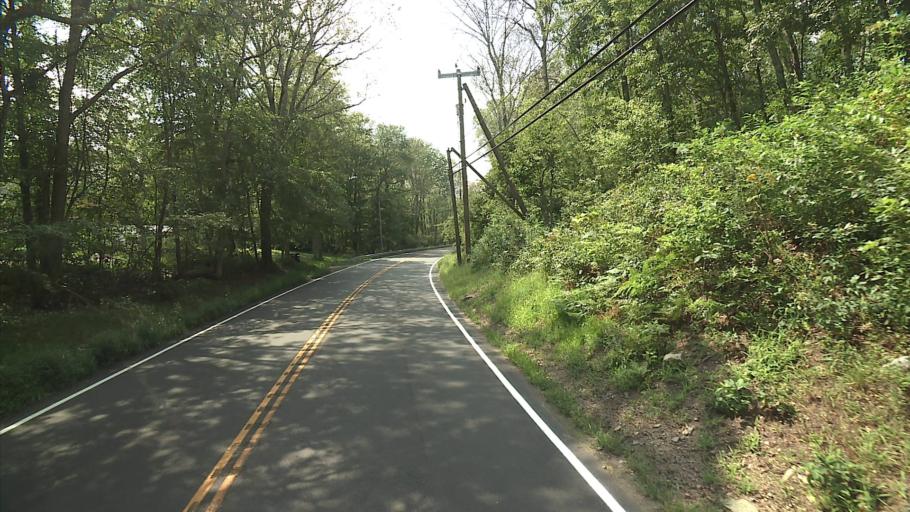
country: US
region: Connecticut
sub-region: New London County
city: Montville Center
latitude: 41.4893
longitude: -72.2426
